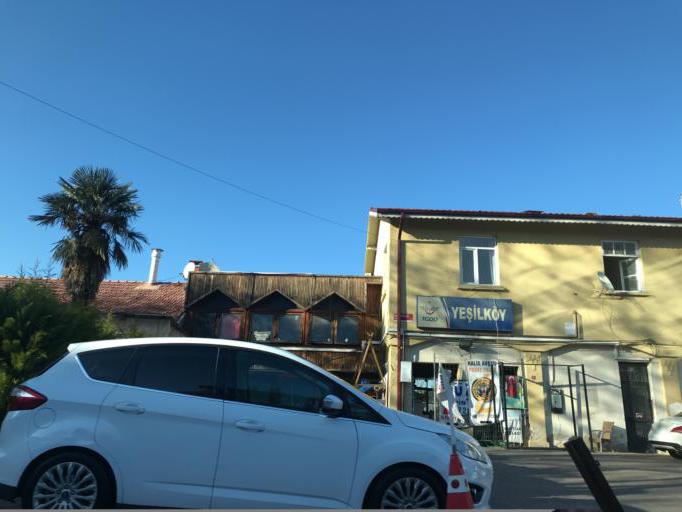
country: TR
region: Istanbul
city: Bahcelievler
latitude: 40.9622
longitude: 28.8252
